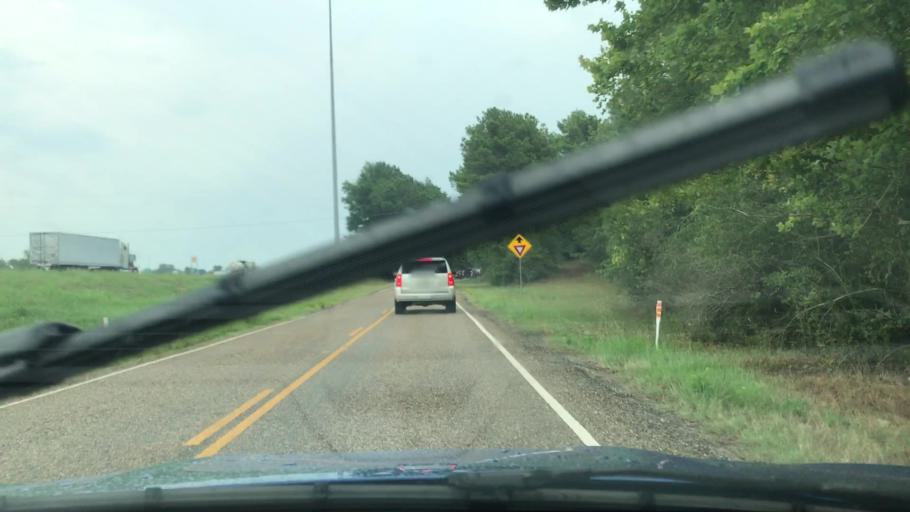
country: US
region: Texas
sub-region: Harrison County
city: Waskom
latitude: 32.4795
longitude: -94.0926
